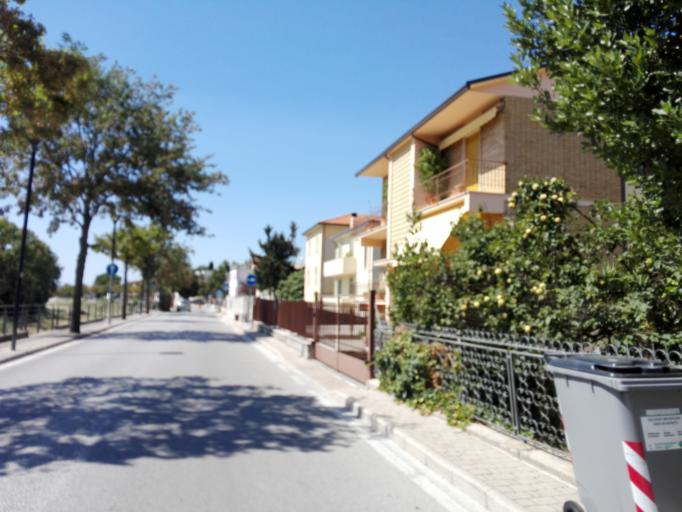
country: IT
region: Umbria
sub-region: Provincia di Perugia
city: Foligno
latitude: 42.9587
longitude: 12.6990
